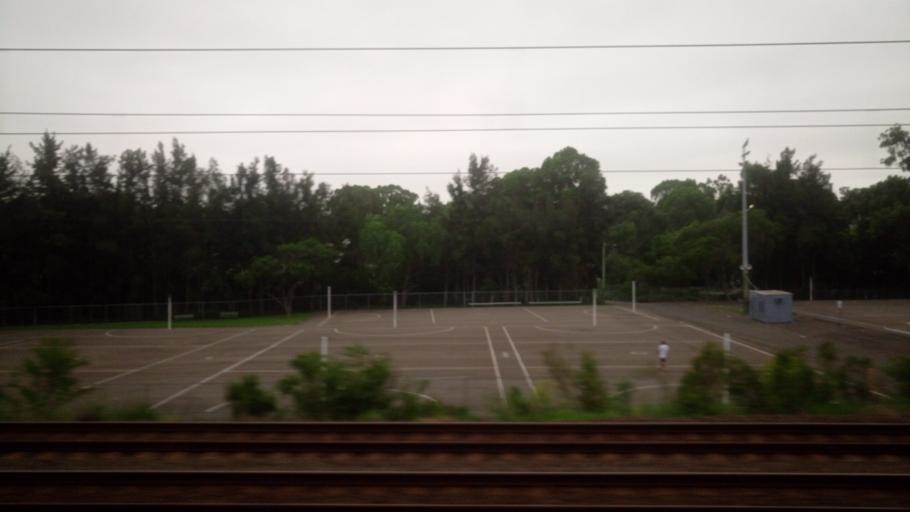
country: AU
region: New South Wales
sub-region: Blacktown
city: Blacktown
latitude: -33.7734
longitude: 150.9184
